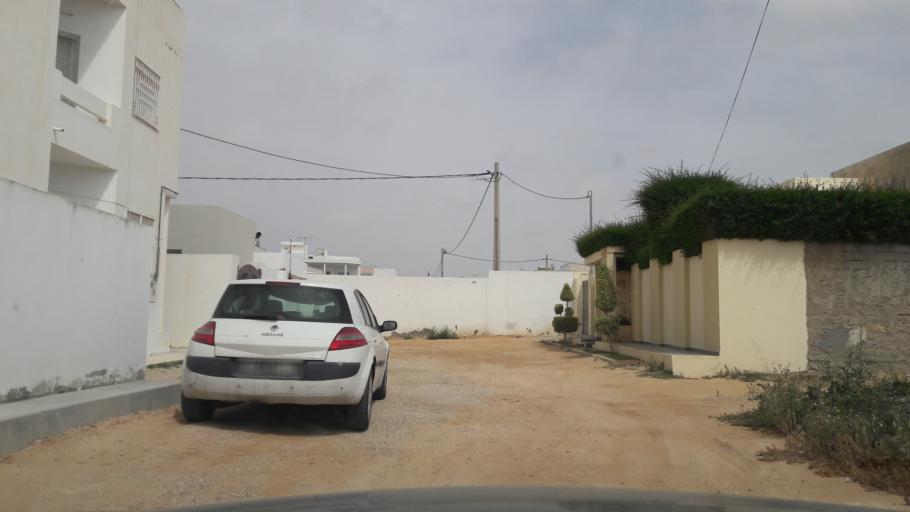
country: TN
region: Safaqis
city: Sfax
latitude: 34.7741
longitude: 10.7567
